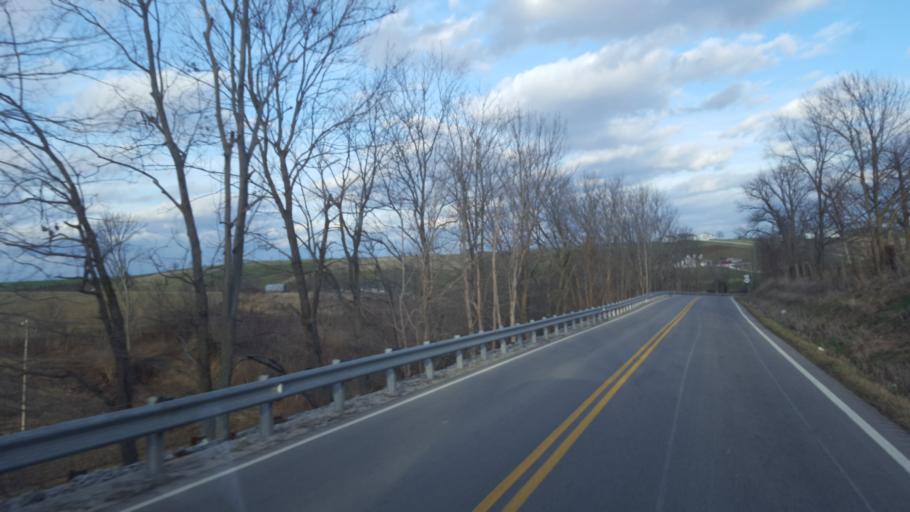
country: US
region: Kentucky
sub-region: Fleming County
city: Flemingsburg
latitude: 38.4519
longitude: -83.6956
